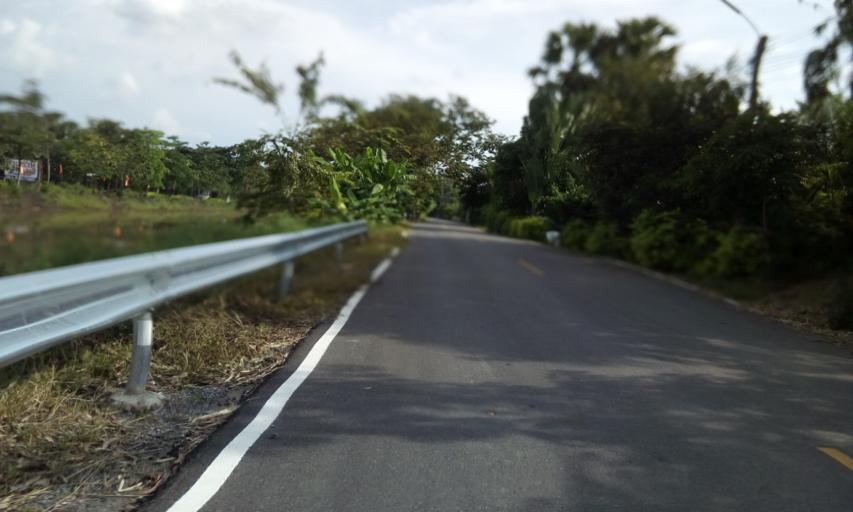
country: TH
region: Pathum Thani
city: Nong Suea
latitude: 14.1208
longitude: 100.8235
